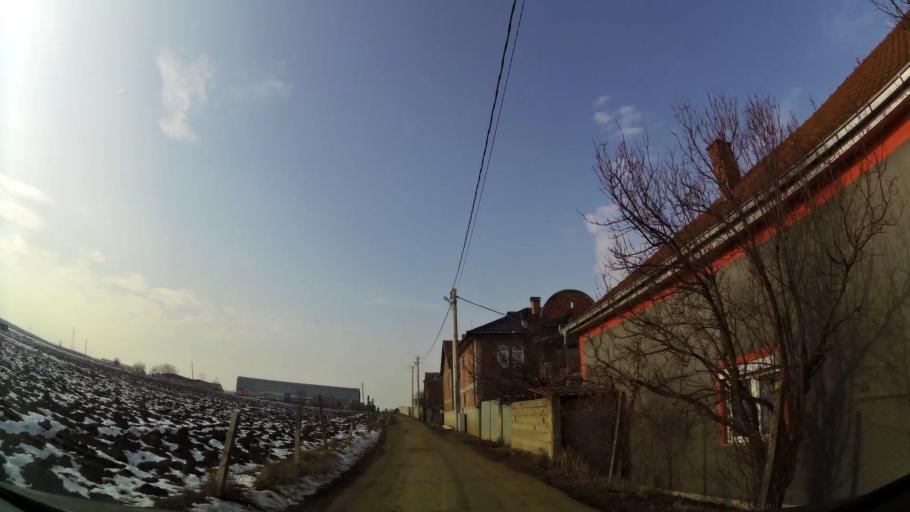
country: MK
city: Creshevo
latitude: 42.0214
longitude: 21.4984
